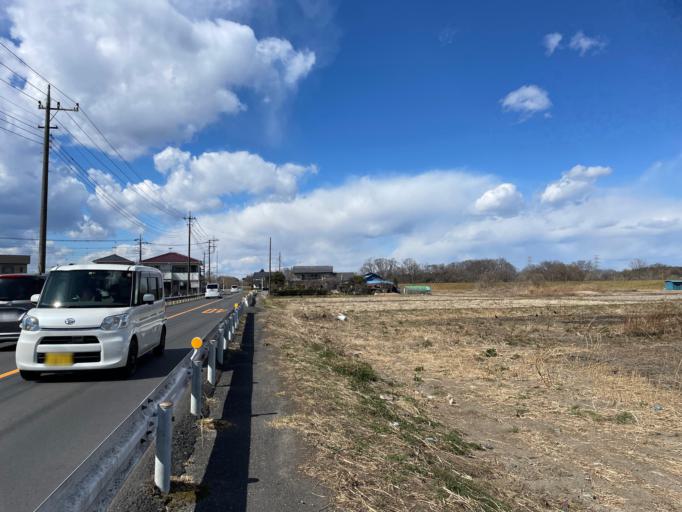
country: JP
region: Saitama
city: Sakado
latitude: 36.0156
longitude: 139.3871
